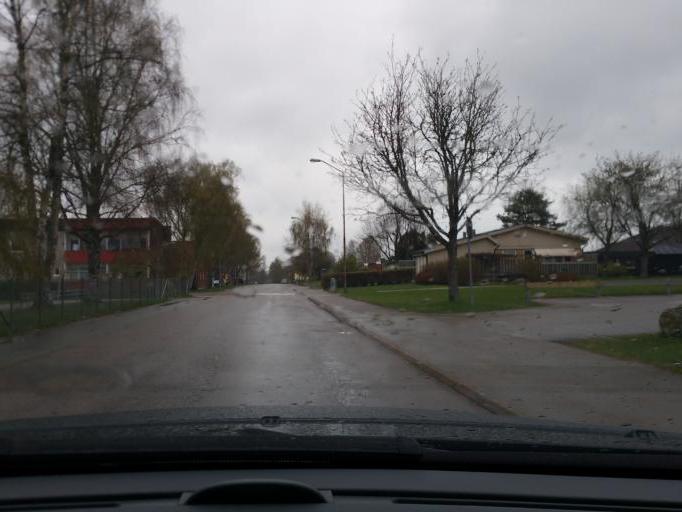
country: SE
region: Kronoberg
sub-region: Vaxjo Kommun
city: Lammhult
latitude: 57.1693
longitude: 14.5875
